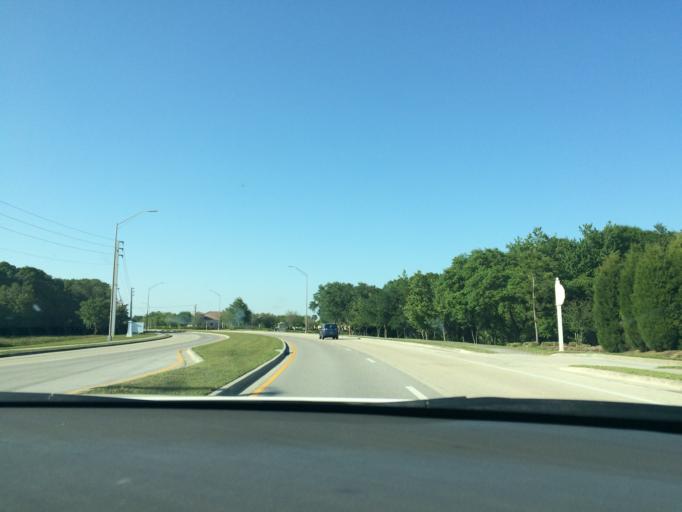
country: US
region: Florida
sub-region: Manatee County
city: Ellenton
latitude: 27.4779
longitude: -82.4333
